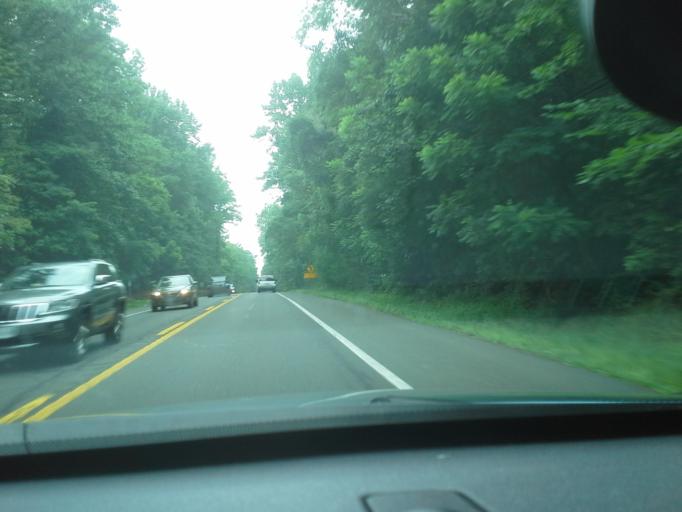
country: US
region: Maryland
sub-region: Calvert County
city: Dunkirk Town Center
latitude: 38.7409
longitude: -76.6300
